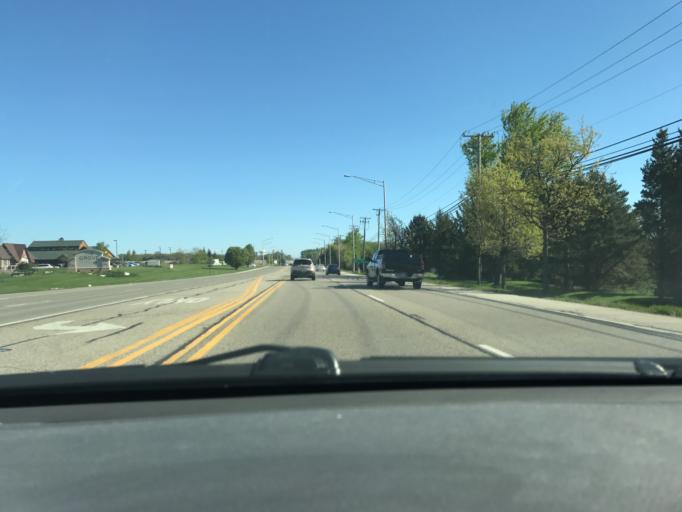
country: US
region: Illinois
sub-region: Kane County
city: Sleepy Hollow
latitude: 42.0919
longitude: -88.3351
